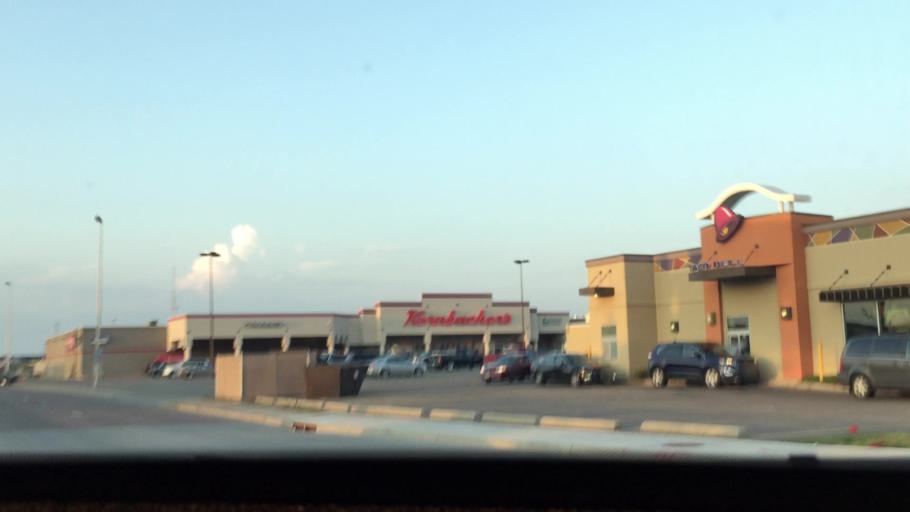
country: US
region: North Dakota
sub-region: Cass County
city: West Fargo
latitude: 46.8619
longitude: -96.8509
